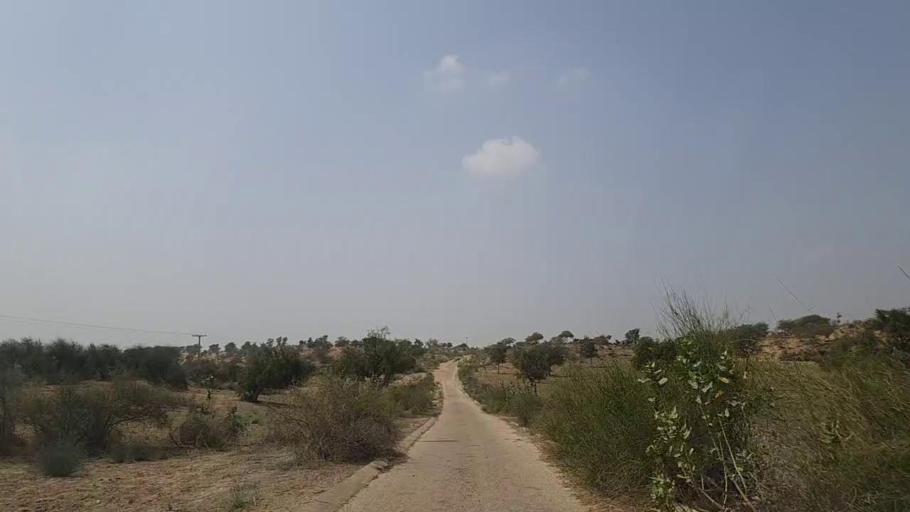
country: PK
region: Sindh
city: Mithi
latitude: 24.7666
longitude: 69.9007
